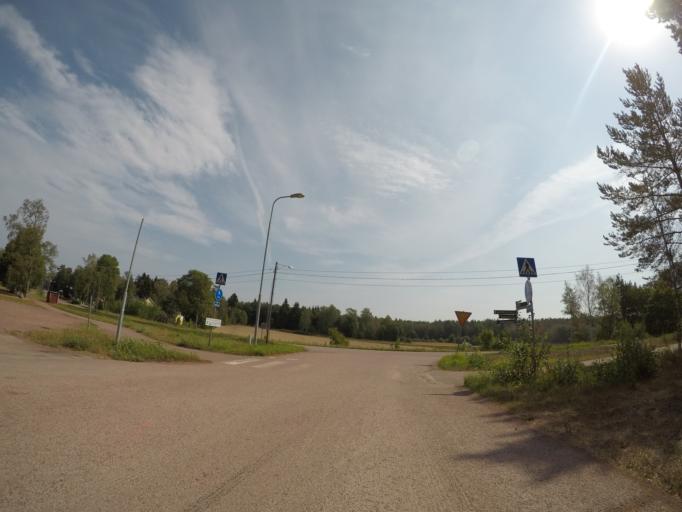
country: AX
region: Alands landsbygd
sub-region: Finstroem
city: Finstroem
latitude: 60.2231
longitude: 19.9806
